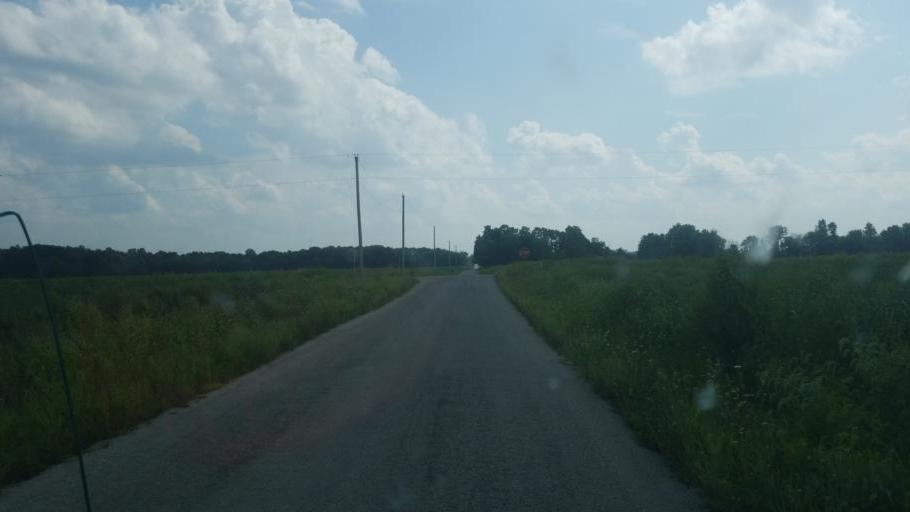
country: US
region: Ohio
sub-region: Huron County
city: New London
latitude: 41.0501
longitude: -82.3752
